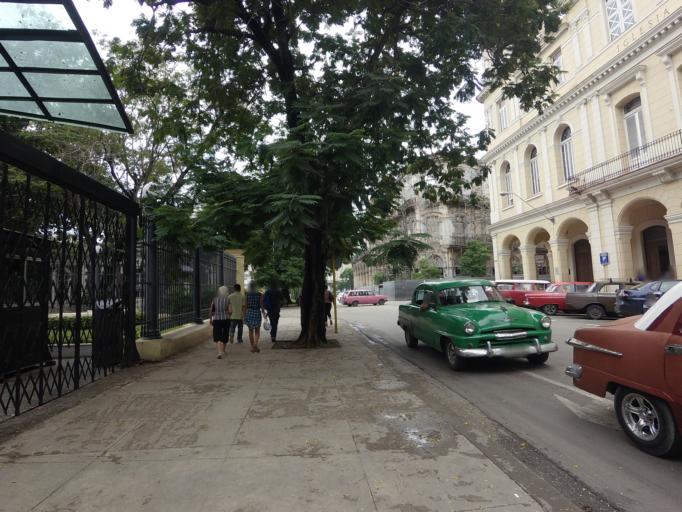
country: CU
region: La Habana
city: La Habana Vieja
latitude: 23.1339
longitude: -82.3578
